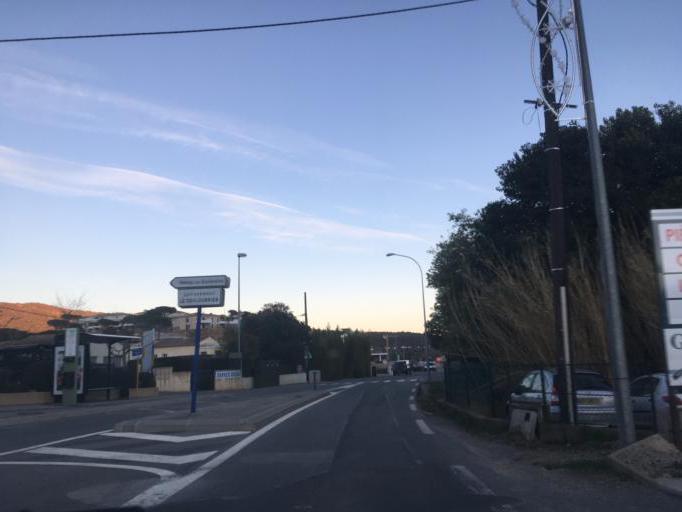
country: FR
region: Provence-Alpes-Cote d'Azur
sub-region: Departement du Var
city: Sainte-Maxime
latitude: 43.3270
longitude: 6.6030
